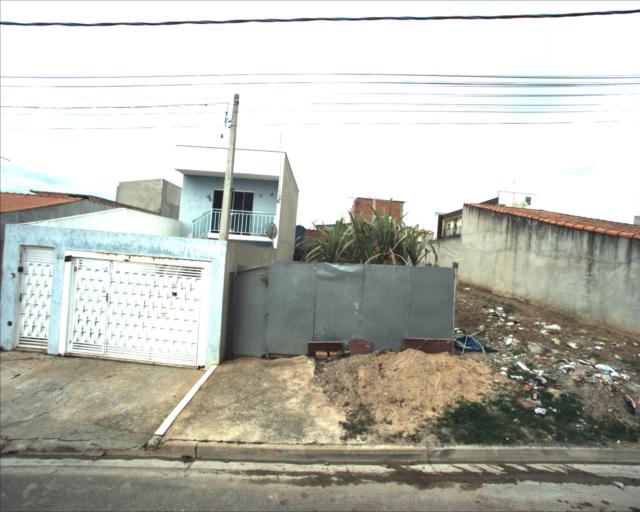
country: BR
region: Sao Paulo
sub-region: Sorocaba
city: Sorocaba
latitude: -23.4365
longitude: -47.4972
